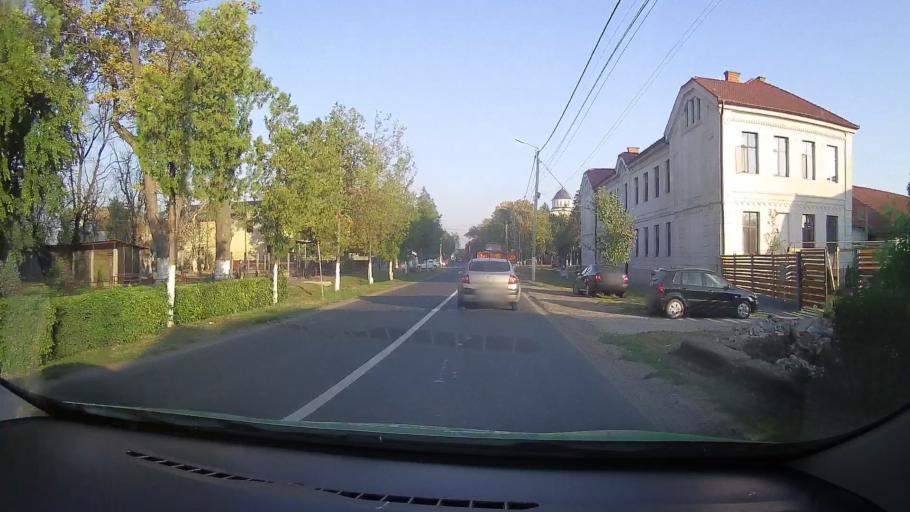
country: RO
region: Arad
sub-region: Comuna Curtici
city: Curtici
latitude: 46.3399
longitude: 21.3084
